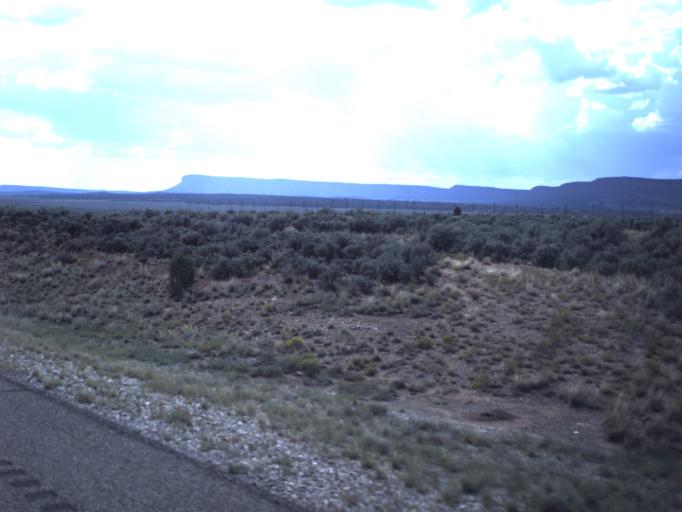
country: US
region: Utah
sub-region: Kane County
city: Kanab
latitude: 37.1350
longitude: -112.0848
